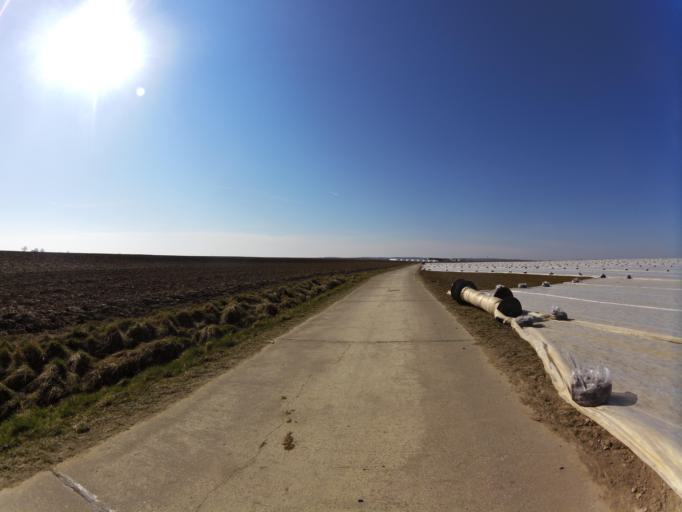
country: DE
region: Bavaria
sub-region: Regierungsbezirk Unterfranken
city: Oberpleichfeld
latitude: 49.8848
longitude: 10.0785
